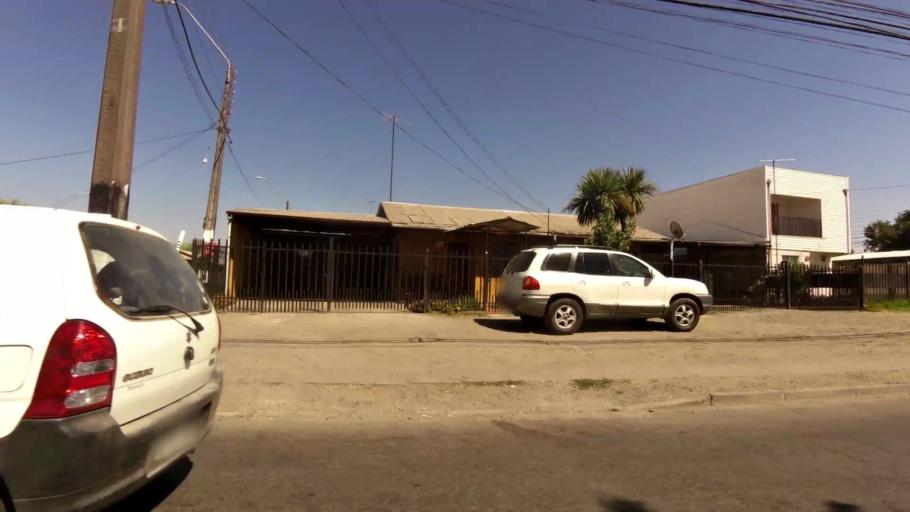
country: CL
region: Maule
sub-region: Provincia de Curico
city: Curico
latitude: -34.9660
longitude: -71.2408
